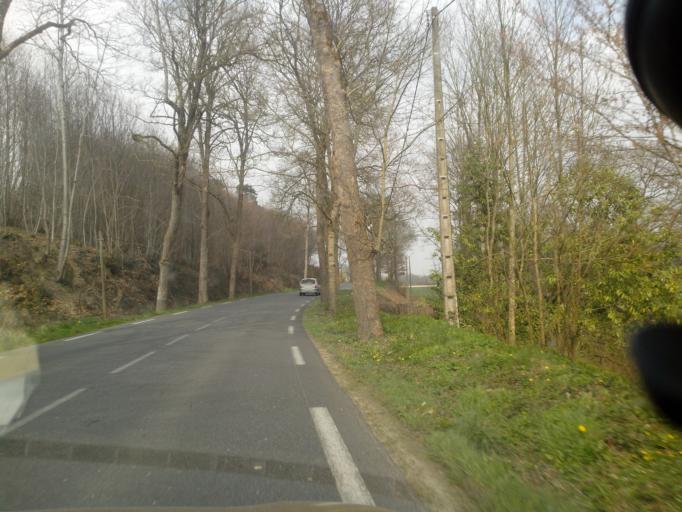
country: FR
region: Brittany
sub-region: Departement des Cotes-d'Armor
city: Caulnes
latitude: 48.2733
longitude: -2.1550
